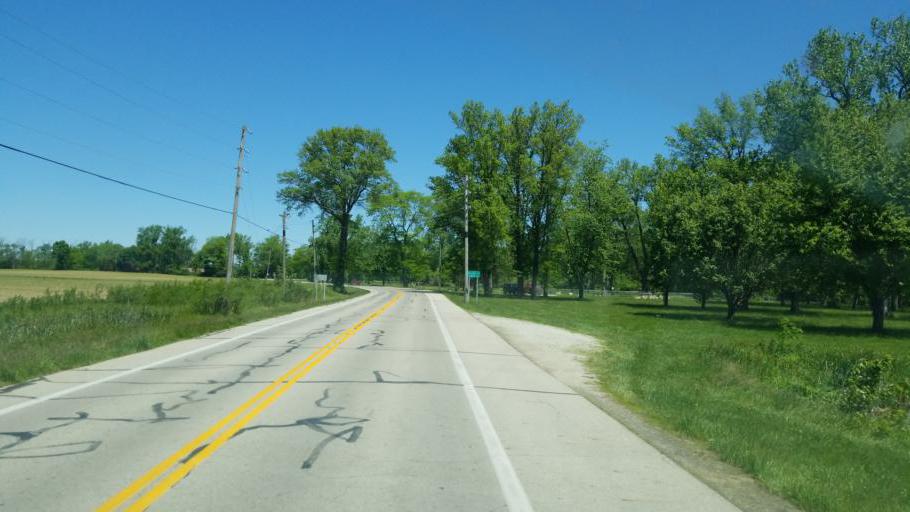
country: US
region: Ohio
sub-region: Auglaize County
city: Minster
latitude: 40.3779
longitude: -84.3585
